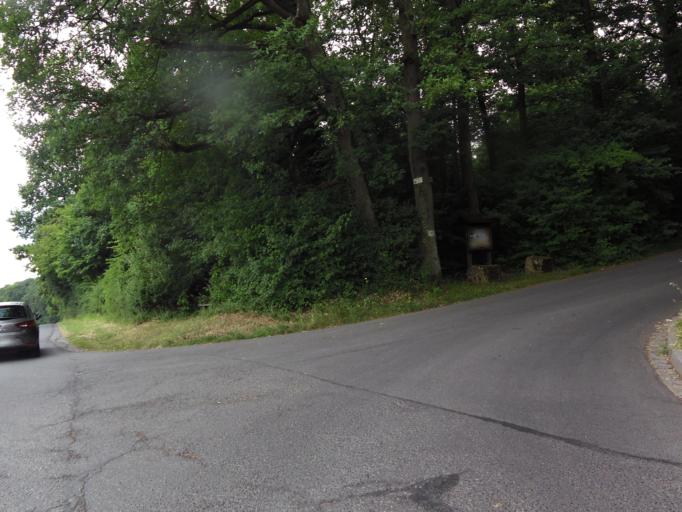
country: DE
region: Bavaria
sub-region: Regierungsbezirk Unterfranken
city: Reichenberg
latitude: 49.7615
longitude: 9.9180
